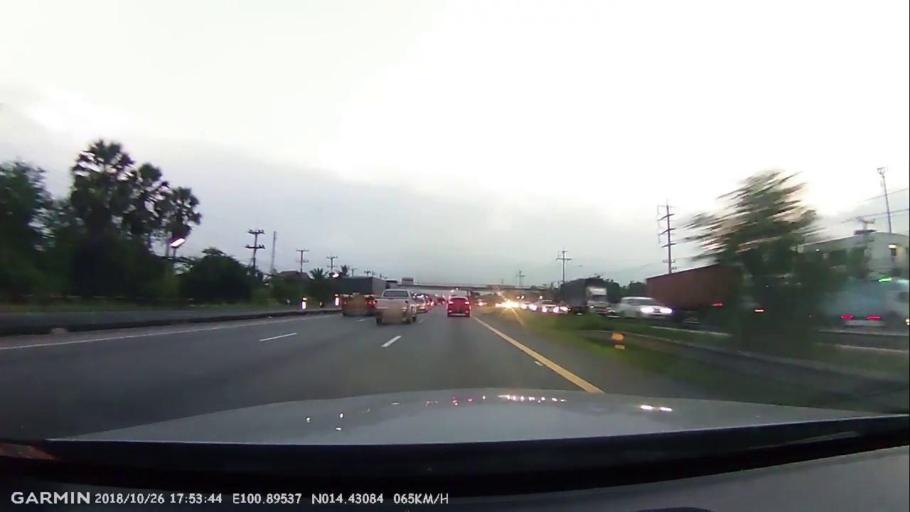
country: TH
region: Sara Buri
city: Nong Khae
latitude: 14.4306
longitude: 100.8953
